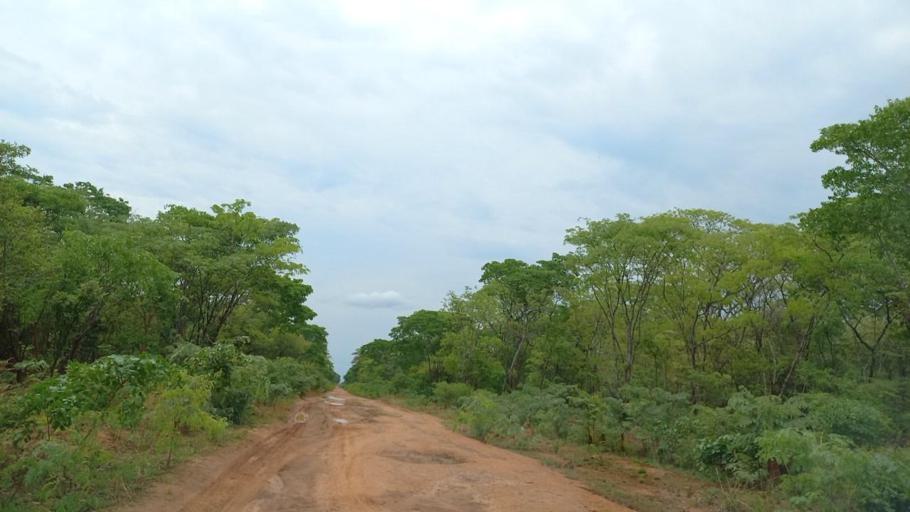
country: ZM
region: North-Western
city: Kalengwa
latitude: -13.6023
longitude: 24.9745
